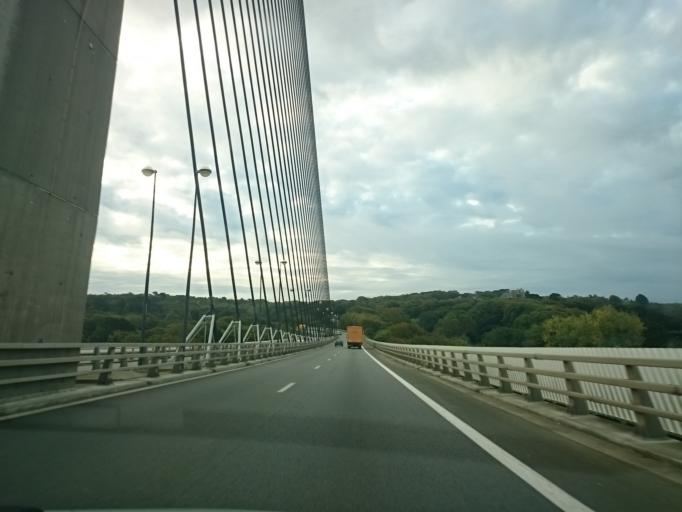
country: FR
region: Brittany
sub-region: Departement du Finistere
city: Le Relecq-Kerhuon
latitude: 48.3870
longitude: -4.3972
